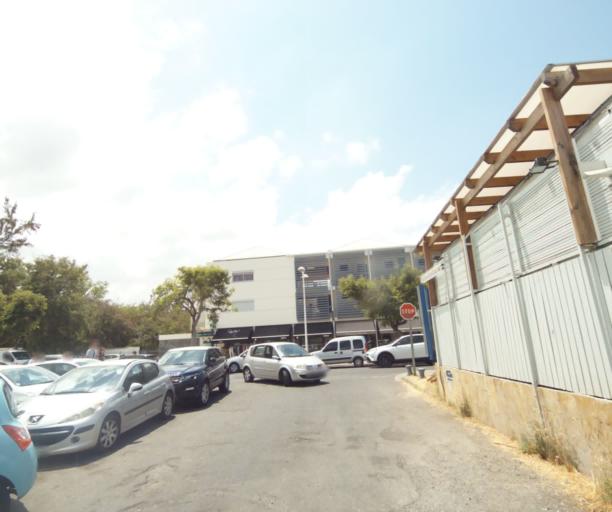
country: RE
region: Reunion
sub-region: Reunion
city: Saint-Paul
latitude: -21.0730
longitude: 55.2232
